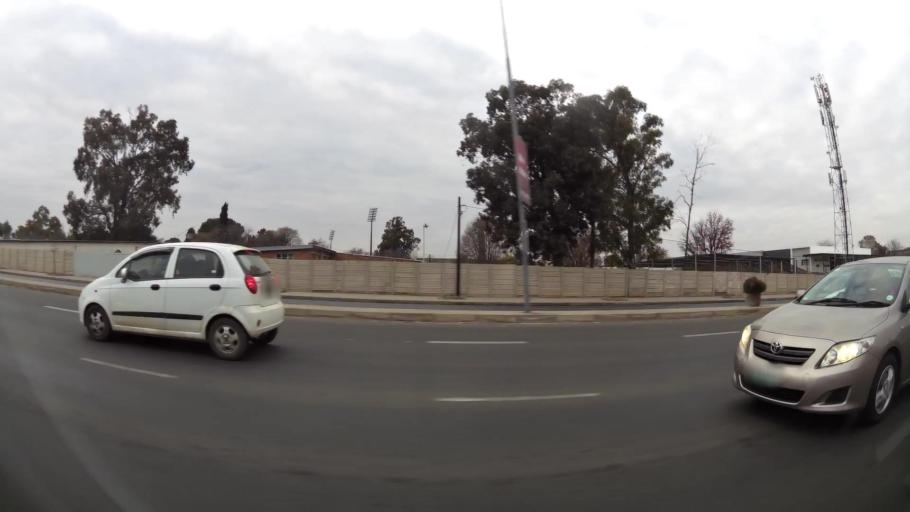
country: ZA
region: Orange Free State
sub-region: Mangaung Metropolitan Municipality
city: Bloemfontein
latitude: -29.1155
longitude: 26.2007
